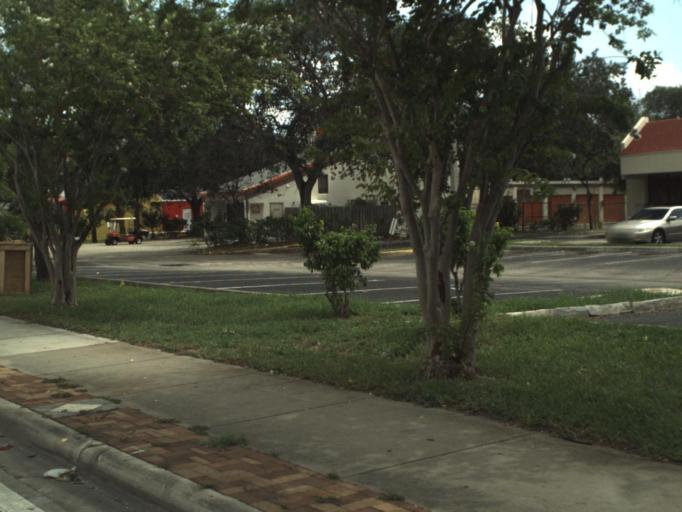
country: US
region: Florida
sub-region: Broward County
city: Lauderhill
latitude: 26.1442
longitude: -80.2026
